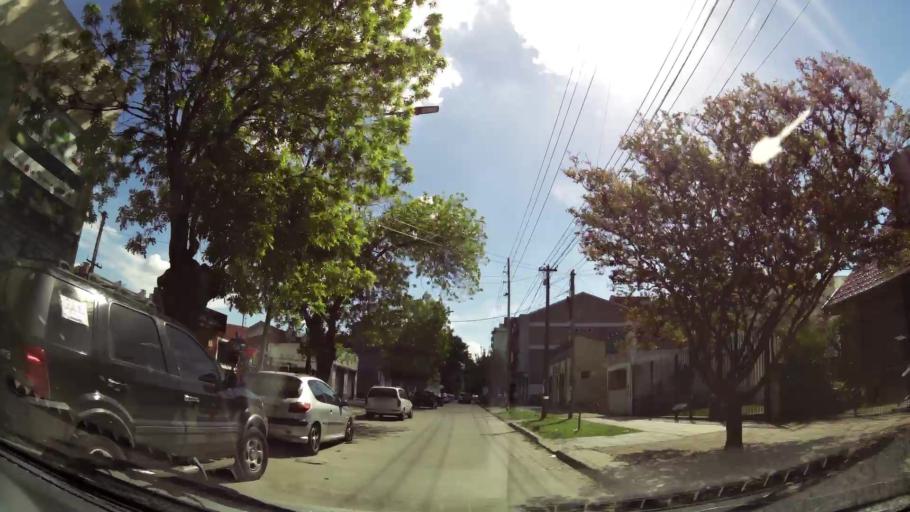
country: AR
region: Buenos Aires
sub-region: Partido de Quilmes
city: Quilmes
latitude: -34.8067
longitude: -58.2738
